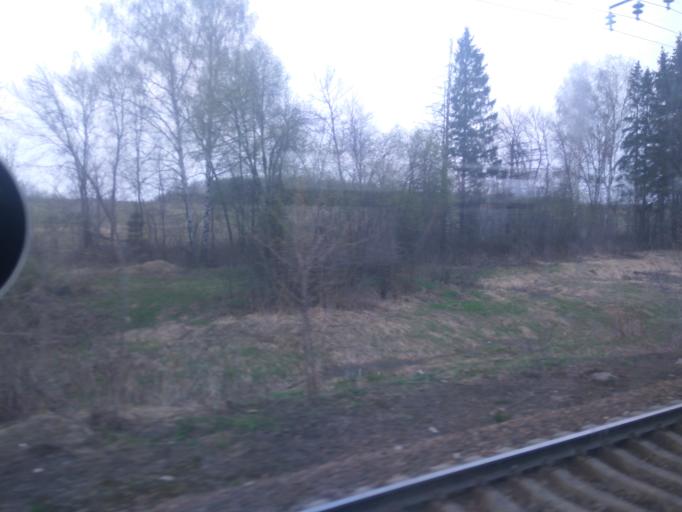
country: RU
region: Vladimir
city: Strunino
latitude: 56.3754
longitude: 38.6342
